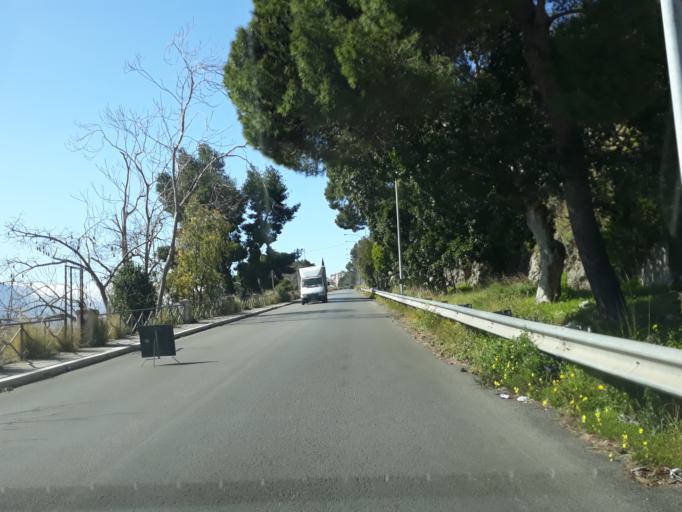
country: IT
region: Sicily
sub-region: Palermo
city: Monreale
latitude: 38.0903
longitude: 13.3014
